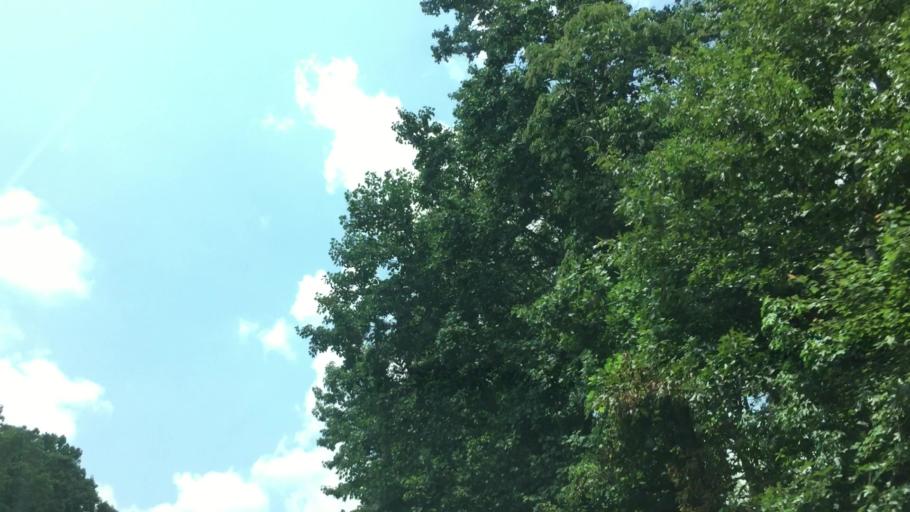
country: US
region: Georgia
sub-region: Carroll County
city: Villa Rica
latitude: 33.6162
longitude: -84.9435
